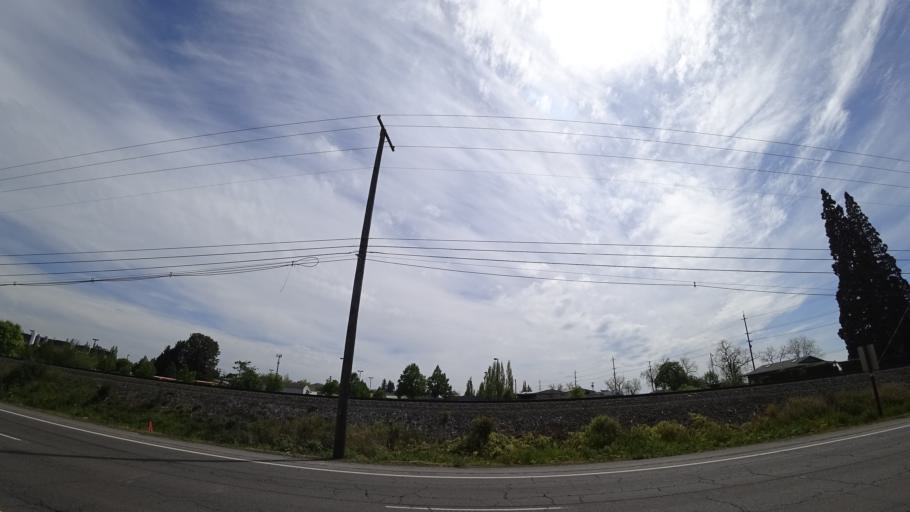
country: US
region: Oregon
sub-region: Washington County
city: Aloha
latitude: 45.4963
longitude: -122.8904
